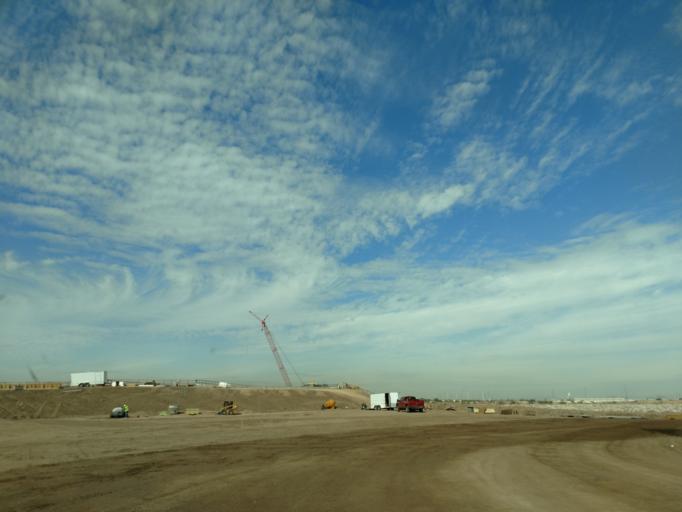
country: US
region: Arizona
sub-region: Maricopa County
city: Laveen
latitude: 33.3947
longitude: -112.1917
